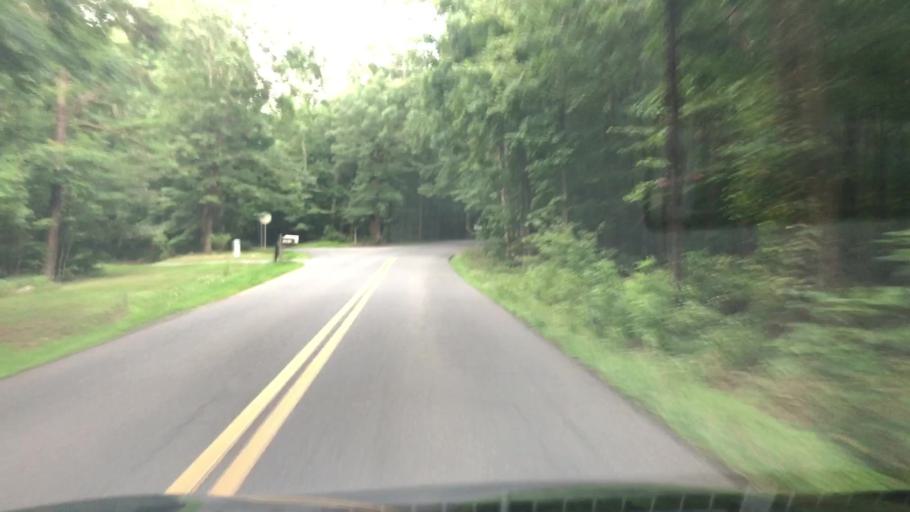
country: US
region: Virginia
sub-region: Fauquier County
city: Bealeton
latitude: 38.5323
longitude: -77.6708
